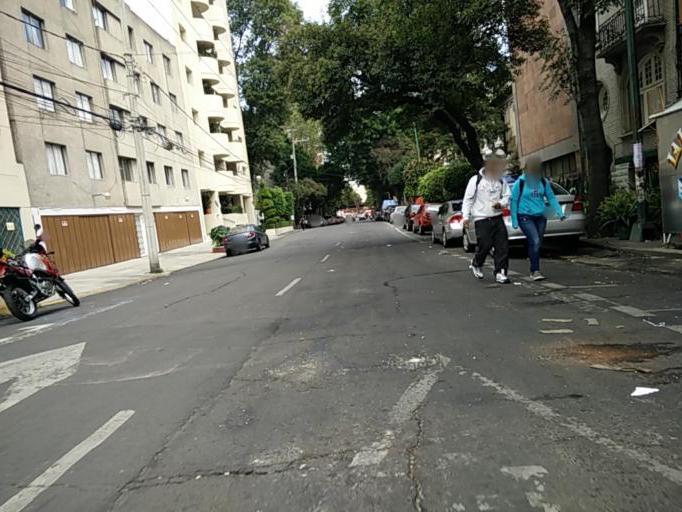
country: MX
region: Mexico City
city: Benito Juarez
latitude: 19.4209
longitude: -99.1618
